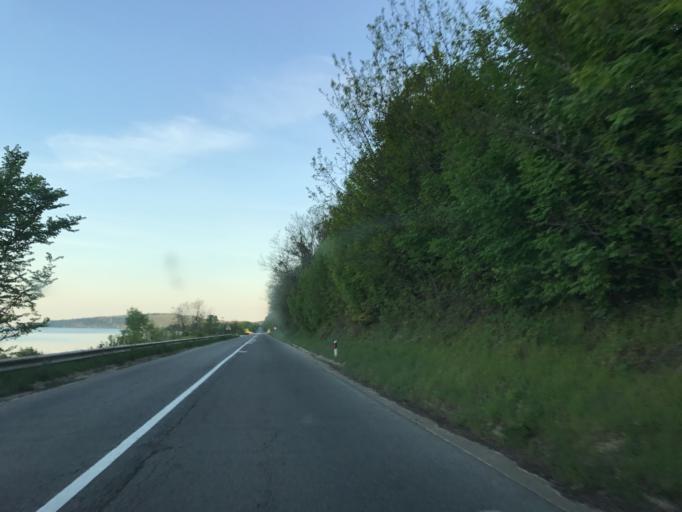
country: RO
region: Mehedinti
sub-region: Comuna Gogosu
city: Ostrovu Mare
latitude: 44.4653
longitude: 22.4504
